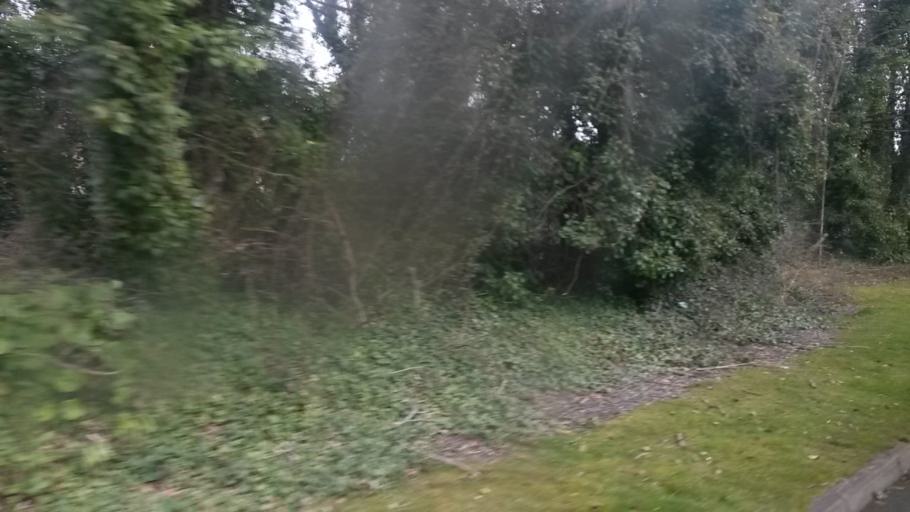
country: IE
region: Leinster
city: Malahide
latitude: 53.4335
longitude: -6.1528
